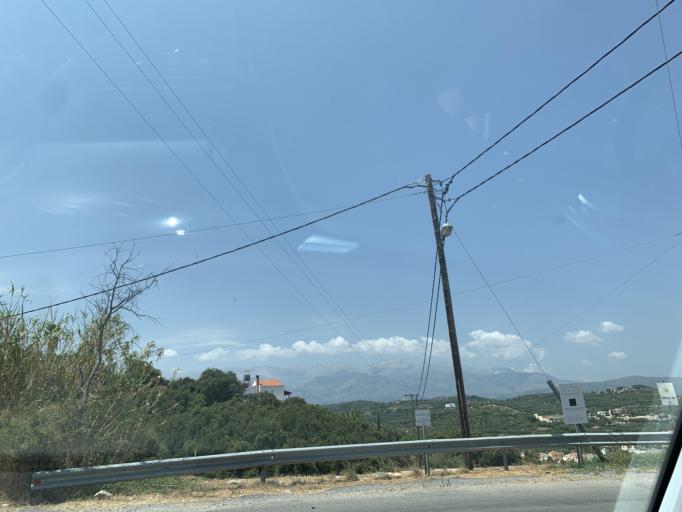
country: GR
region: Crete
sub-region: Nomos Chanias
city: Kalivai
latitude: 35.4482
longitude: 24.2061
